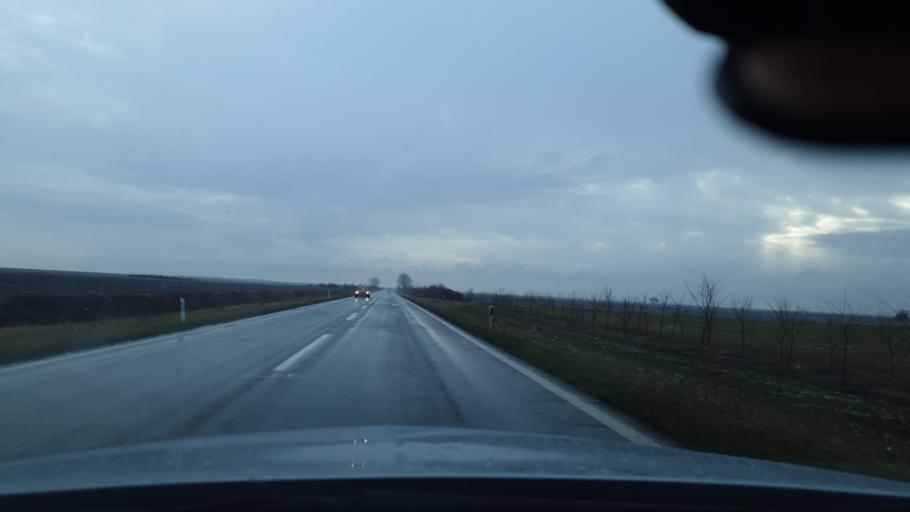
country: RS
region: Autonomna Pokrajina Vojvodina
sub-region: Juznobanatski Okrug
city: Pancevo
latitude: 44.8413
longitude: 20.7974
